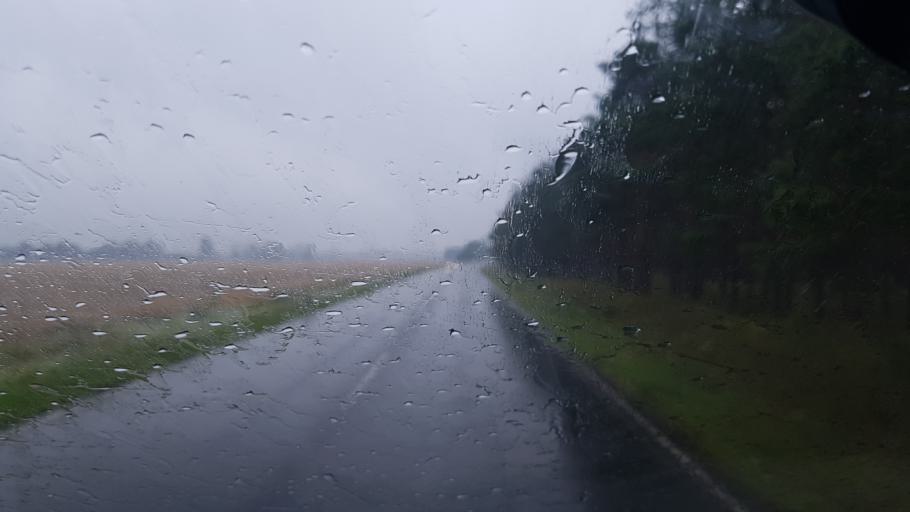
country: DE
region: Brandenburg
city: Baruth
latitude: 52.0532
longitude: 13.5789
